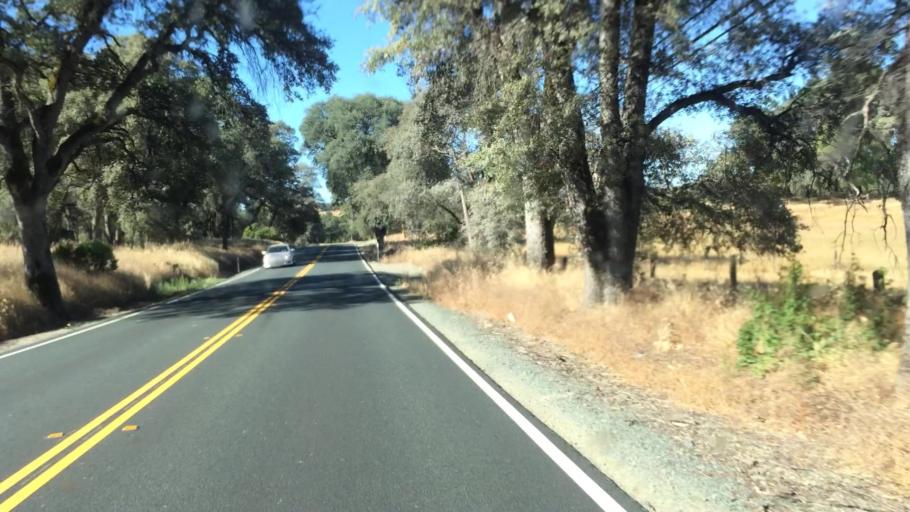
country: US
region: California
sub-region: El Dorado County
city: Deer Park
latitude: 38.6748
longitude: -120.8509
